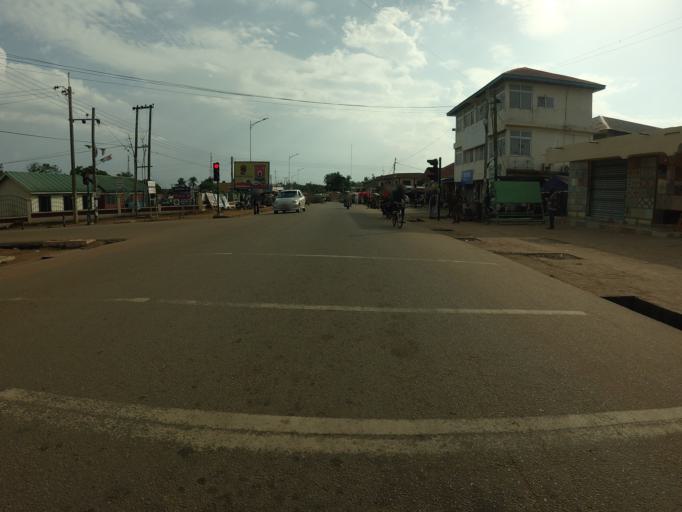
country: GH
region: Volta
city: Hohoe
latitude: 7.1504
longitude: 0.4706
